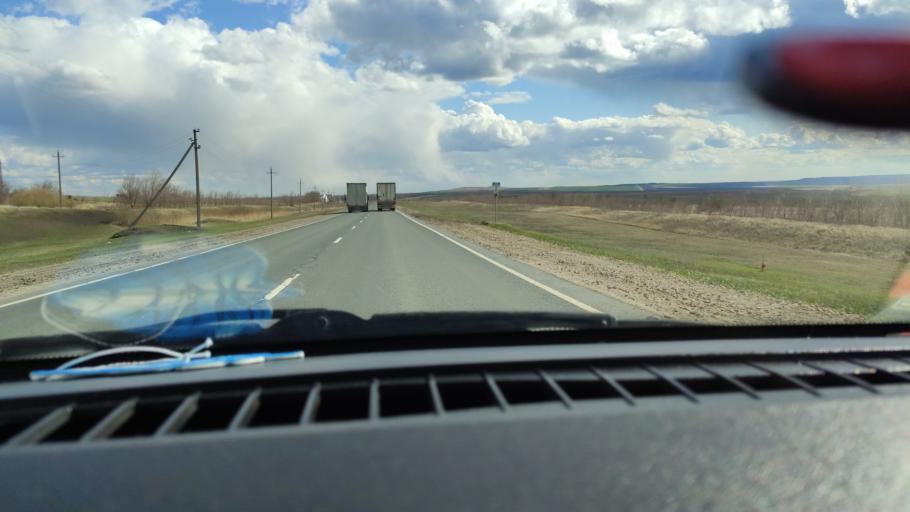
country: RU
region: Saratov
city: Alekseyevka
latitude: 52.2948
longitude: 47.9287
